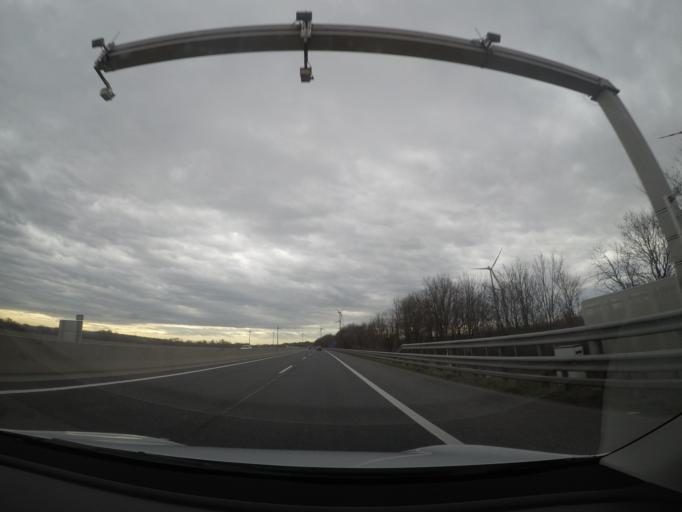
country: AT
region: Lower Austria
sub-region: Politischer Bezirk Baden
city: Ebreichsdorf
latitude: 47.9596
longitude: 16.3661
